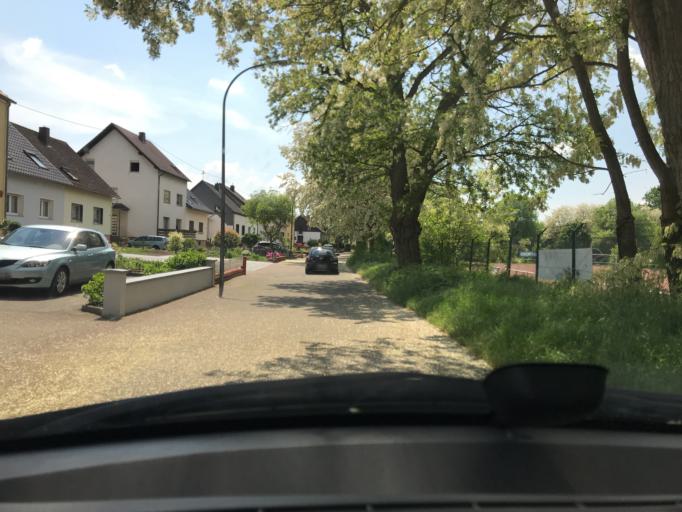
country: DE
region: Saarland
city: Saarlouis
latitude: 49.3341
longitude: 6.7599
